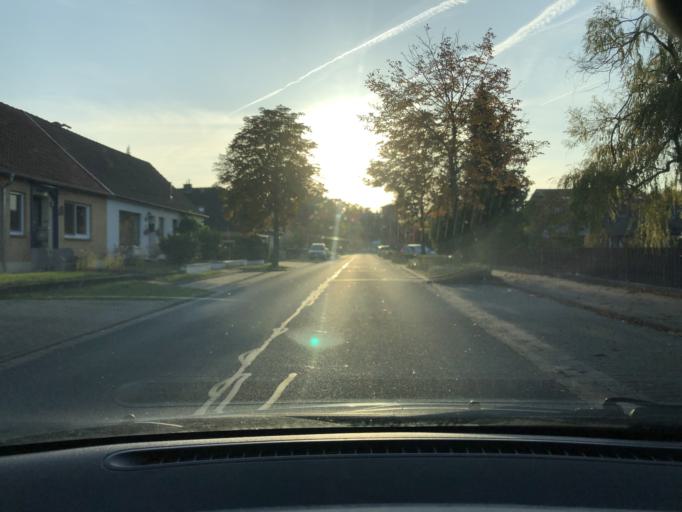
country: DE
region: Lower Saxony
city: Hitzacker
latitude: 53.1402
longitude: 11.0414
